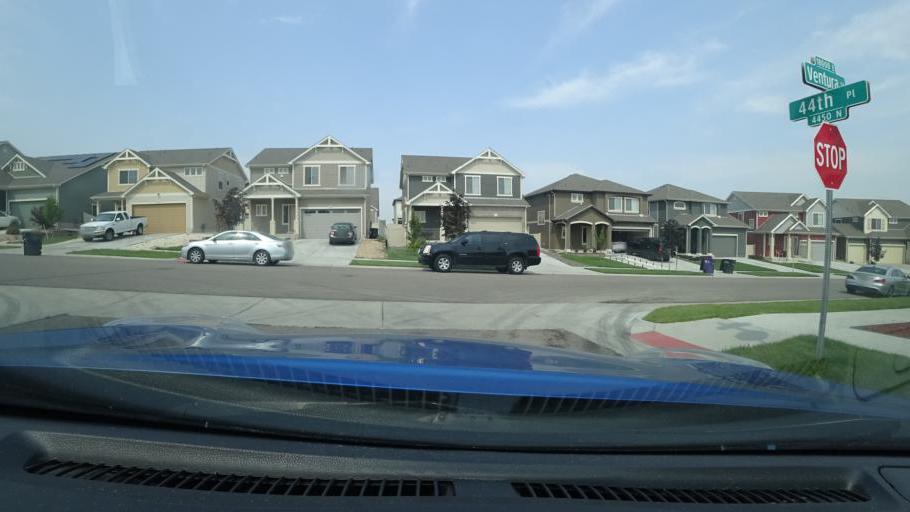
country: US
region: Colorado
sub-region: Adams County
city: Aurora
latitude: 39.7774
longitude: -104.7789
